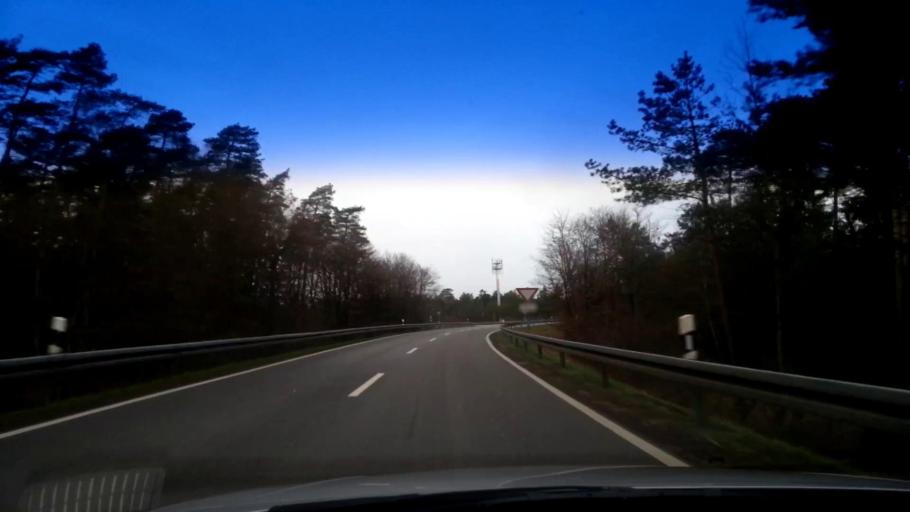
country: DE
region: Bavaria
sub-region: Upper Franconia
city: Strullendorf
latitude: 49.8579
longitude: 10.9720
